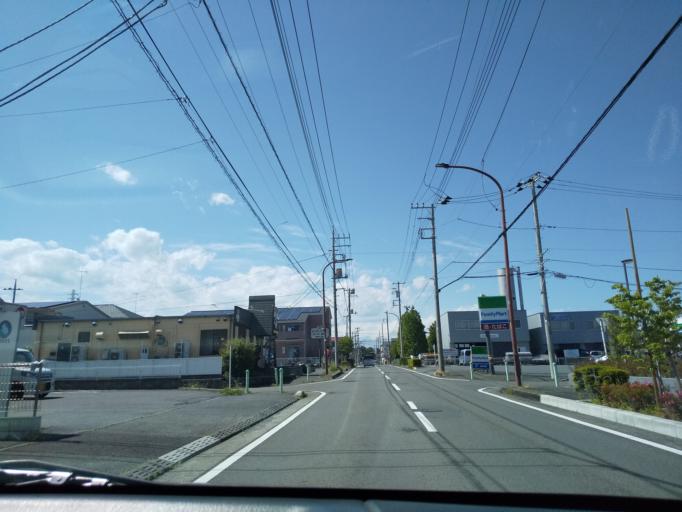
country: JP
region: Kanagawa
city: Zama
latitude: 35.5318
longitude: 139.3764
